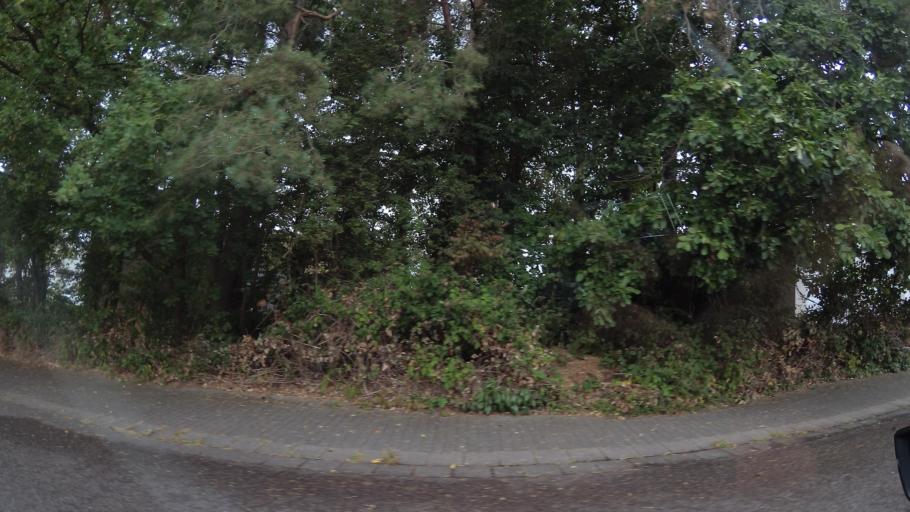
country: DE
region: Saarland
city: Sankt Ingbert
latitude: 49.2683
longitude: 7.1697
